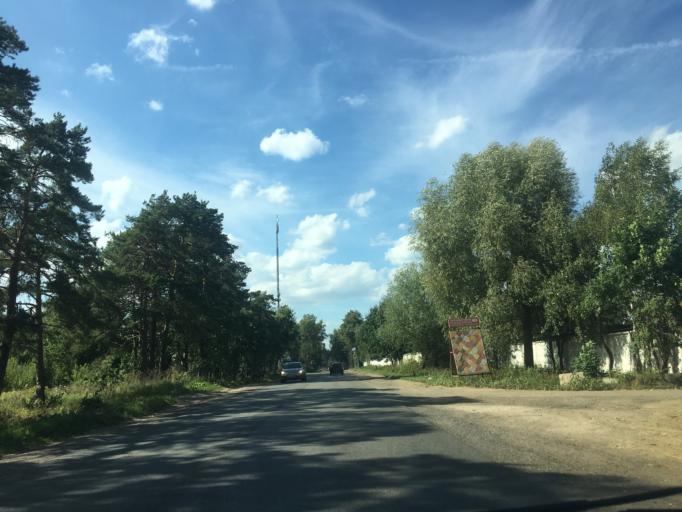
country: RU
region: Moskovskaya
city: Vidnoye
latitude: 55.5293
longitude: 37.6709
